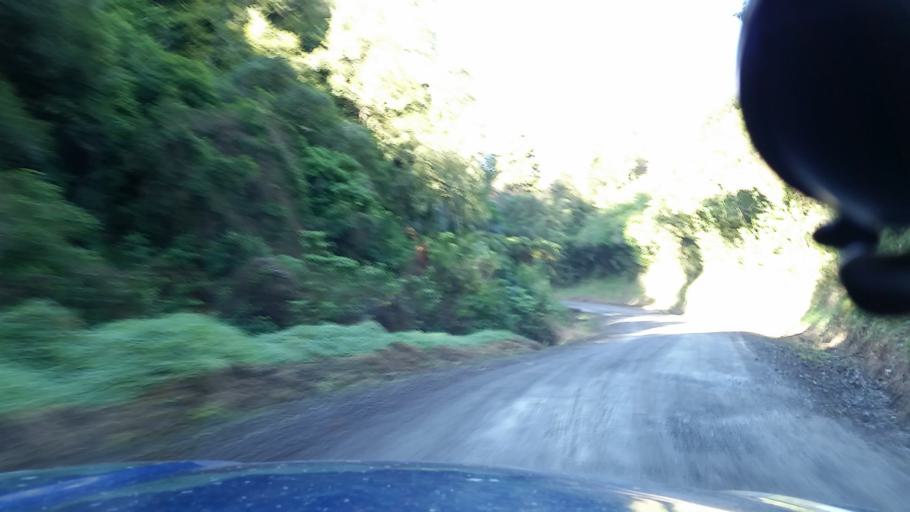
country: NZ
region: Taranaki
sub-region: New Plymouth District
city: Waitara
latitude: -39.0608
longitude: 174.7855
